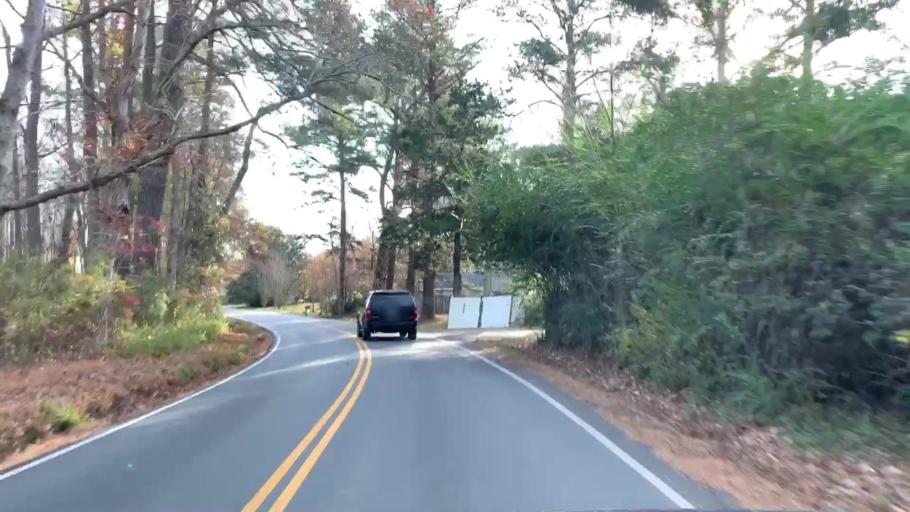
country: US
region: Virginia
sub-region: City of Virginia Beach
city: Virginia Beach
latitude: 36.6908
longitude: -76.0334
